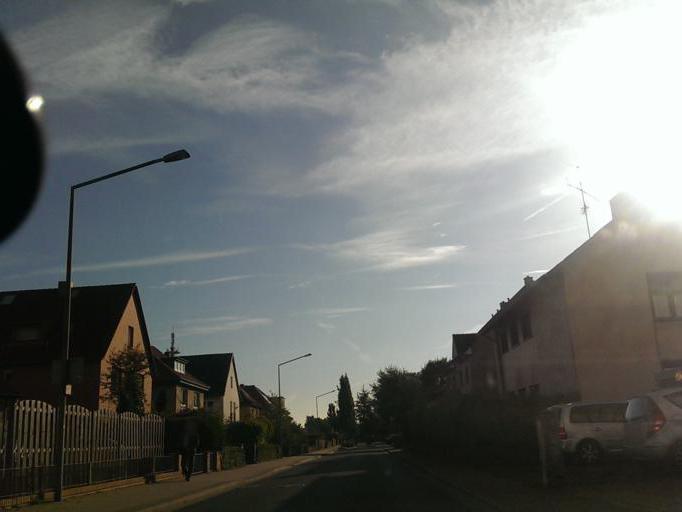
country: DE
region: Lower Saxony
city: Wunstorf
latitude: 52.4262
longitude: 9.4503
